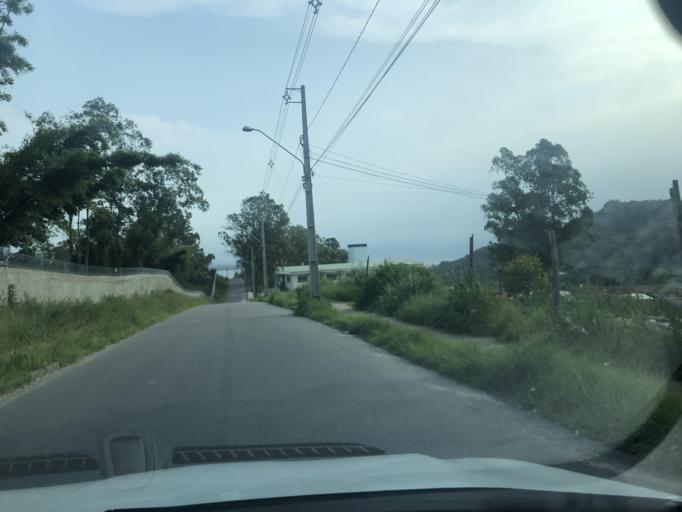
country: BR
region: Santa Catarina
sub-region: Florianopolis
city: Carvoeira
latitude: -27.5997
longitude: -48.5328
